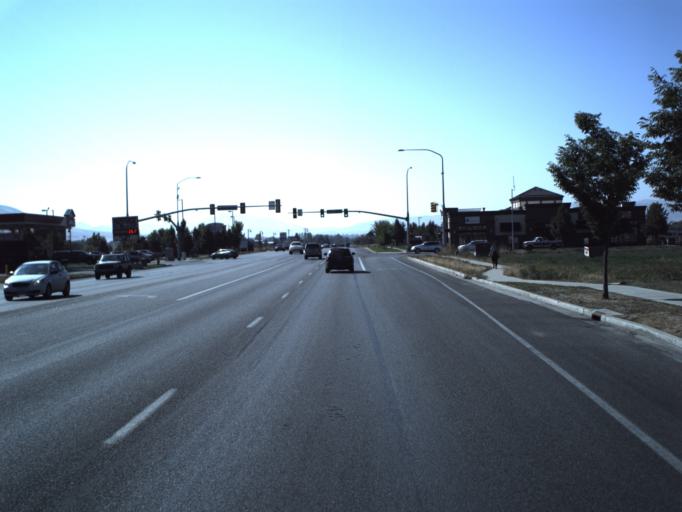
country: US
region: Utah
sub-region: Cache County
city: River Heights
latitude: 41.7113
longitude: -111.8347
